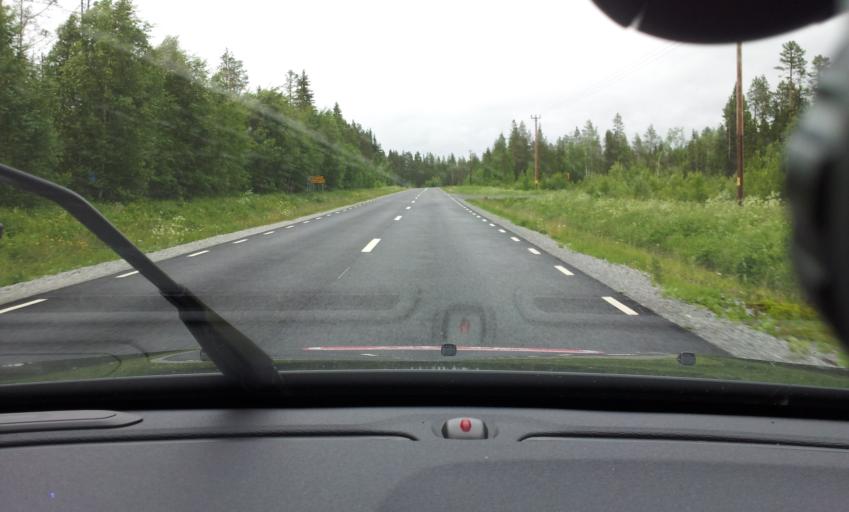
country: SE
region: Jaemtland
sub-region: OEstersunds Kommun
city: Lit
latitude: 63.7380
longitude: 14.7694
